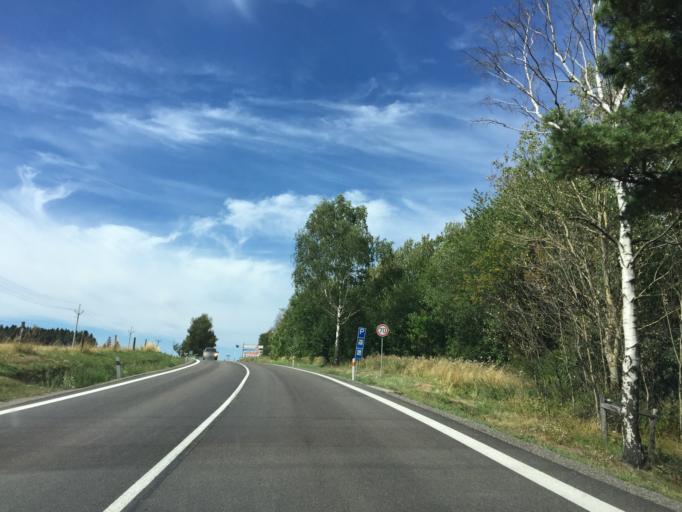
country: CZ
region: Central Bohemia
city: Votice
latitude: 49.5983
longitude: 14.6614
